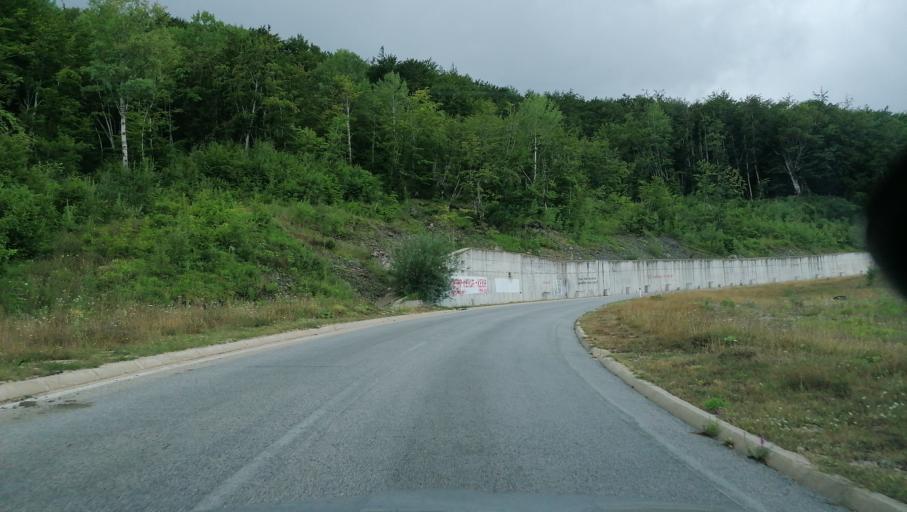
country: BA
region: Republika Srpska
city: Gacko
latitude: 43.2486
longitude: 18.6281
